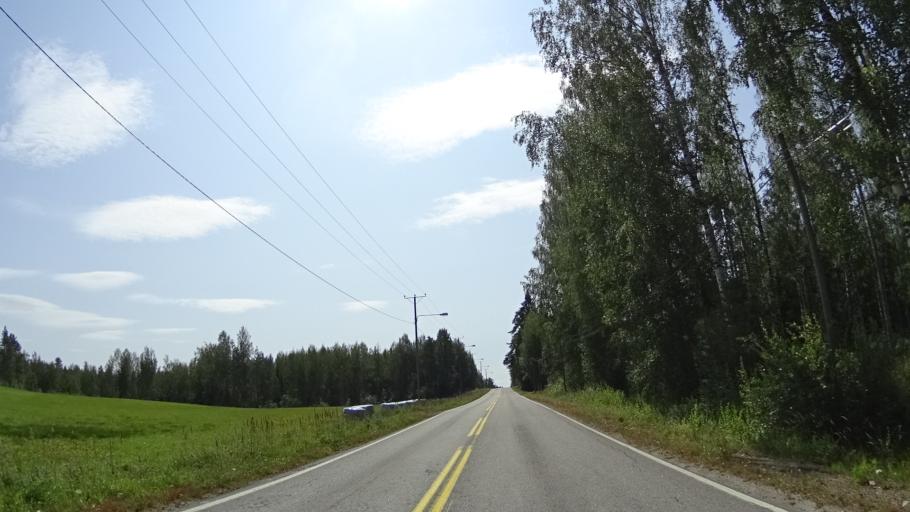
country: FI
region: Pirkanmaa
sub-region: Ylae-Pirkanmaa
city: Maenttae
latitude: 61.8974
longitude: 24.7936
